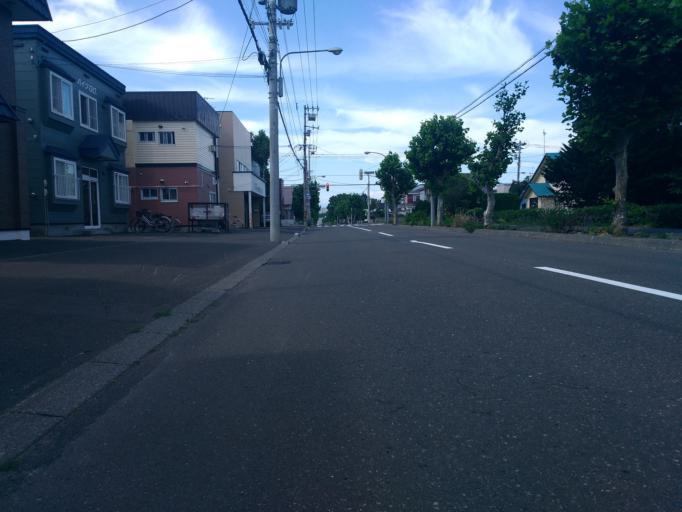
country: JP
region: Hokkaido
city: Ebetsu
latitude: 43.0805
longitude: 141.5058
